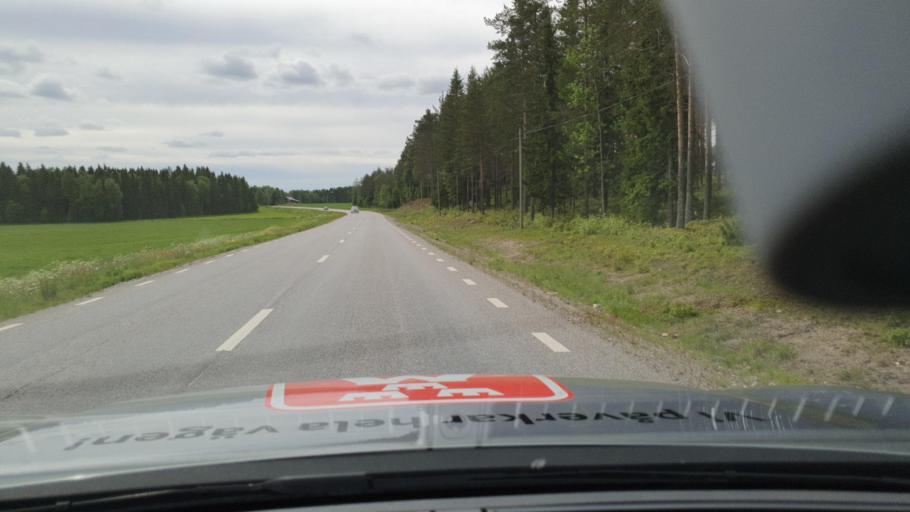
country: SE
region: Norrbotten
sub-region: Kalix Kommun
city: Kalix
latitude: 65.9486
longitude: 23.4545
